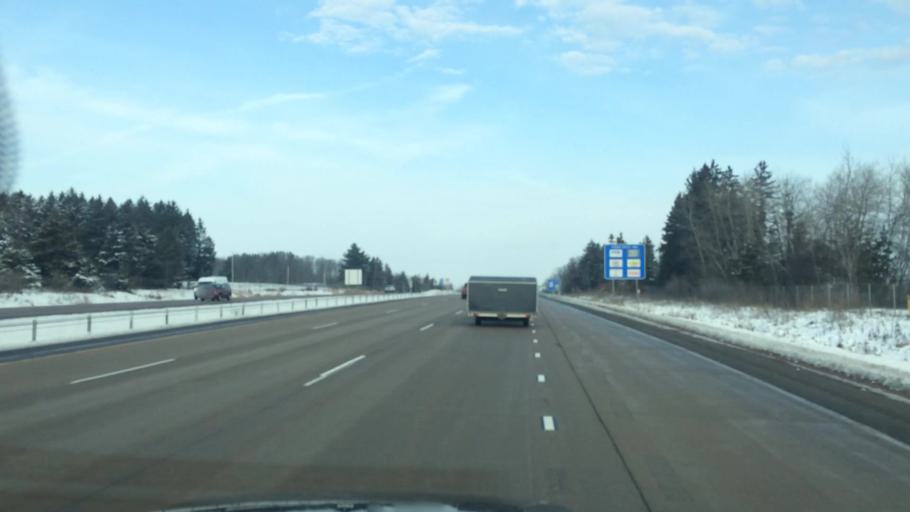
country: US
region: Wisconsin
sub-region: Marathon County
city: Rib Mountain
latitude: 44.9167
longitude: -89.6543
